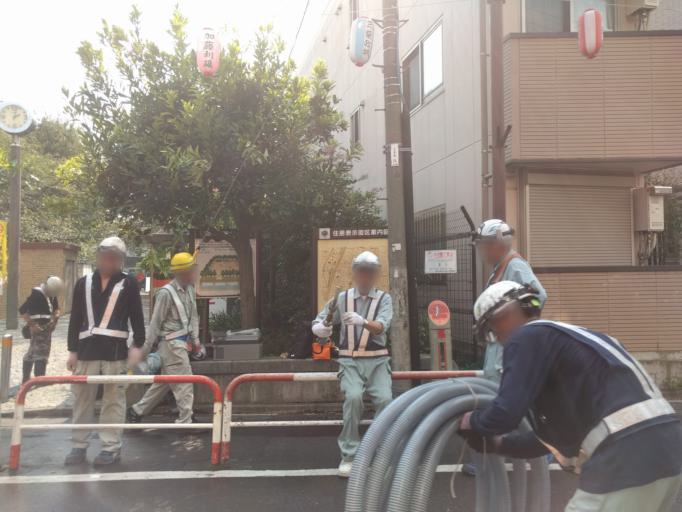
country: JP
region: Tokyo
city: Tokyo
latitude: 35.6821
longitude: 139.6747
